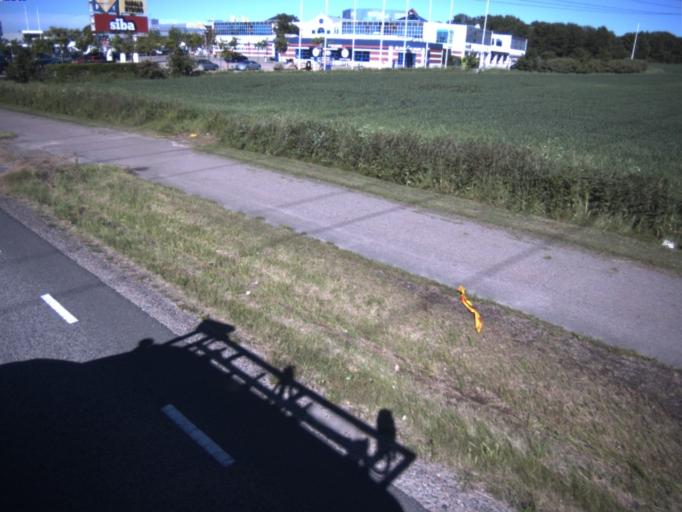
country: SE
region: Skane
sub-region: Helsingborg
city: Odakra
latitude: 56.0891
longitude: 12.7449
